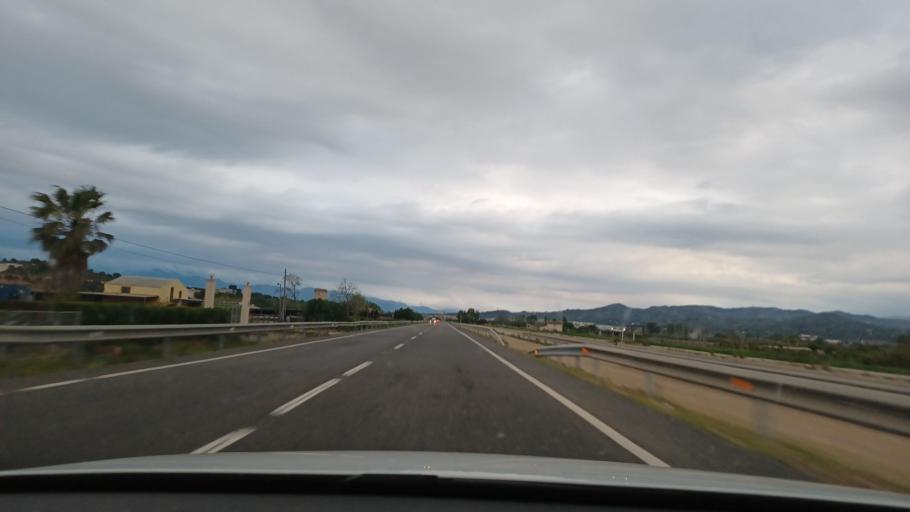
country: ES
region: Catalonia
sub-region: Provincia de Tarragona
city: Amposta
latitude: 40.7366
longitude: 0.5670
